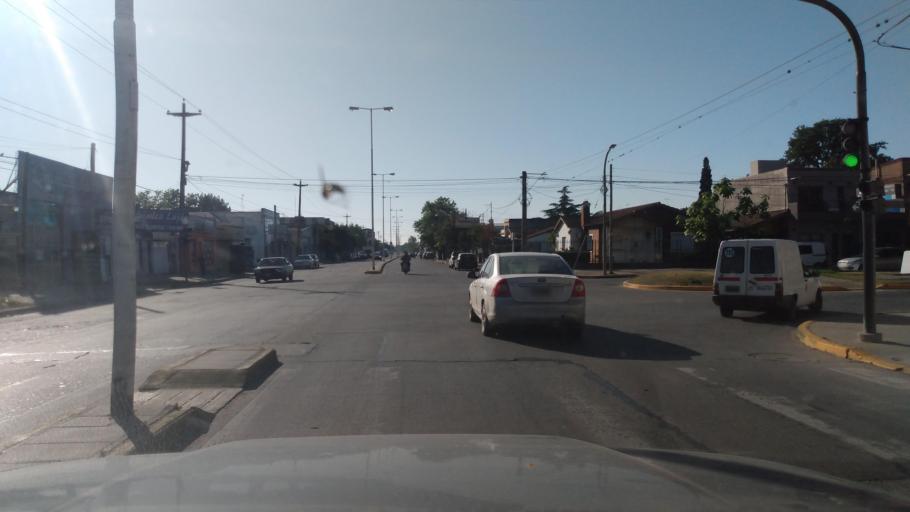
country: AR
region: Buenos Aires
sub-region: Partido de Lujan
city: Lujan
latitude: -34.5610
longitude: -59.1084
